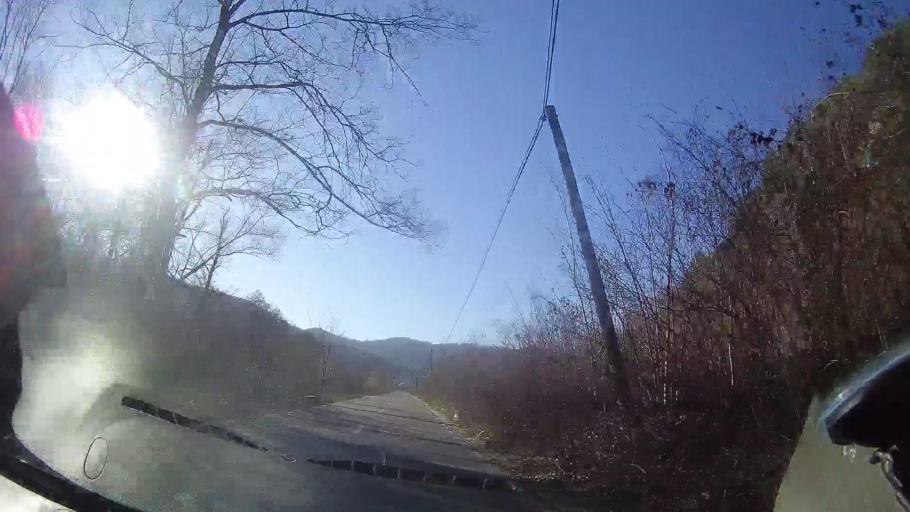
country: RO
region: Bihor
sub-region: Comuna Bratca
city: Bratca
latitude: 46.9250
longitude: 22.6284
